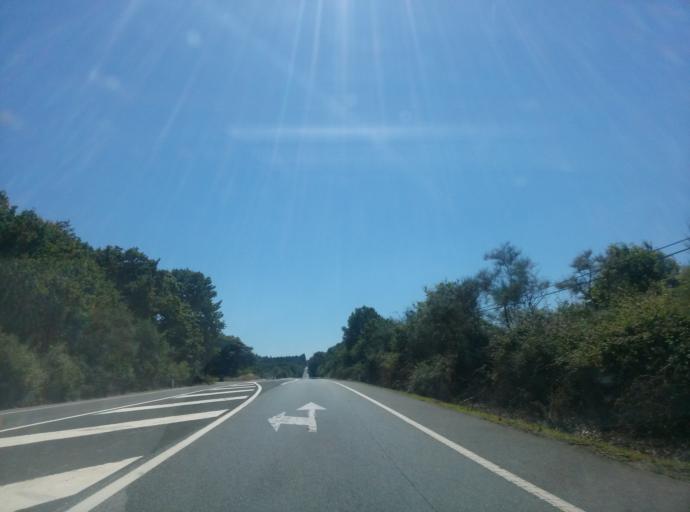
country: ES
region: Galicia
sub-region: Provincia de Lugo
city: Mos
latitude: 43.1076
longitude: -7.4598
